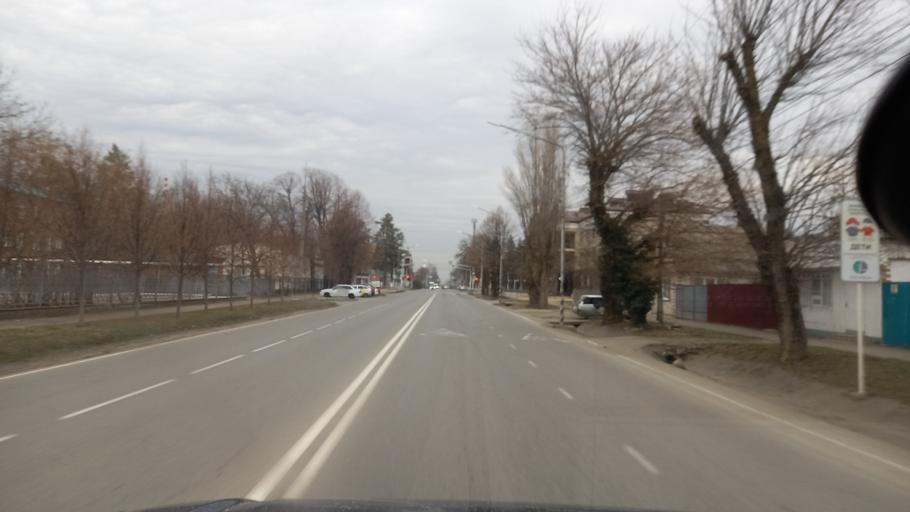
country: RU
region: Adygeya
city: Maykop
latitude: 44.5990
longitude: 40.1098
